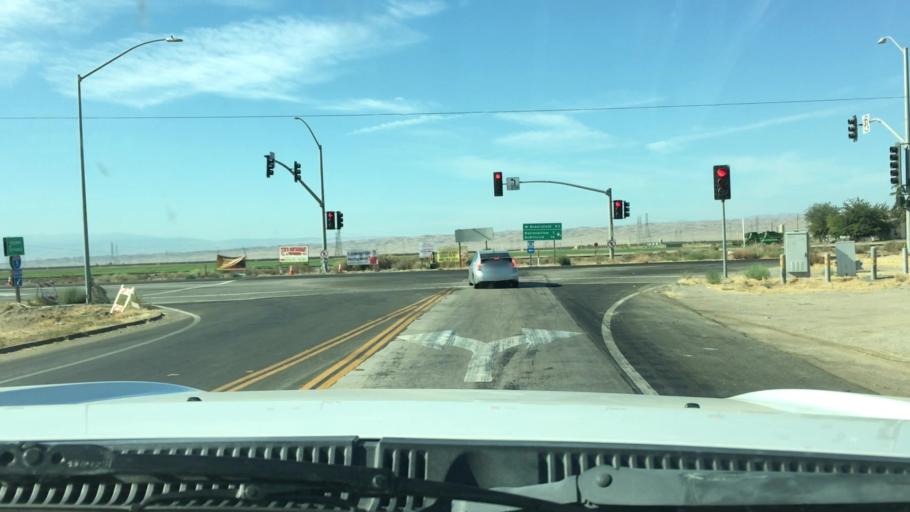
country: US
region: California
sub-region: Kern County
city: Buttonwillow
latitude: 35.3996
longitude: -119.4006
